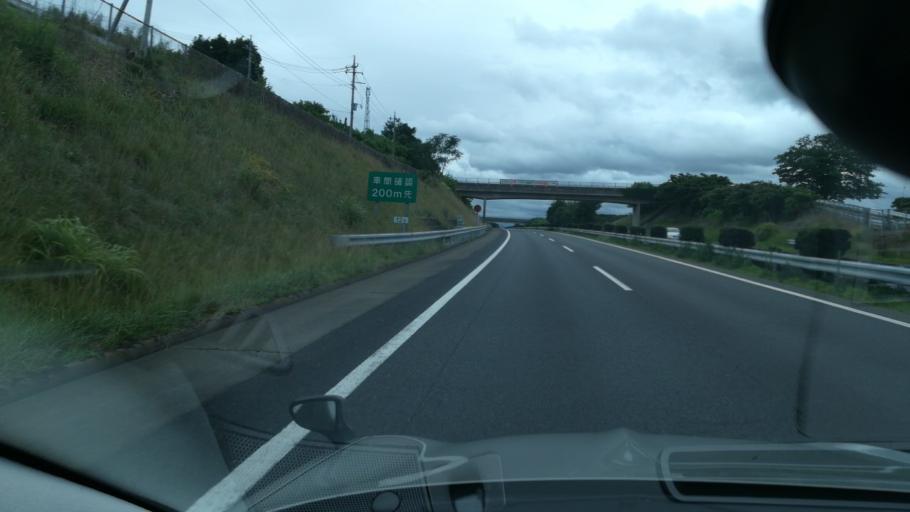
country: JP
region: Gunma
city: Yoshii
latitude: 36.2412
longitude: 138.9745
